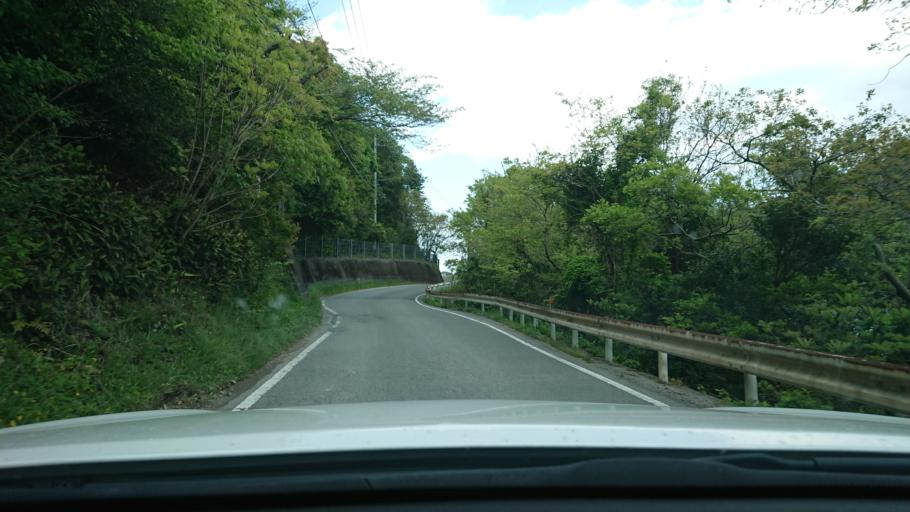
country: JP
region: Tokushima
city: Komatsushimacho
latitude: 33.9853
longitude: 134.5446
